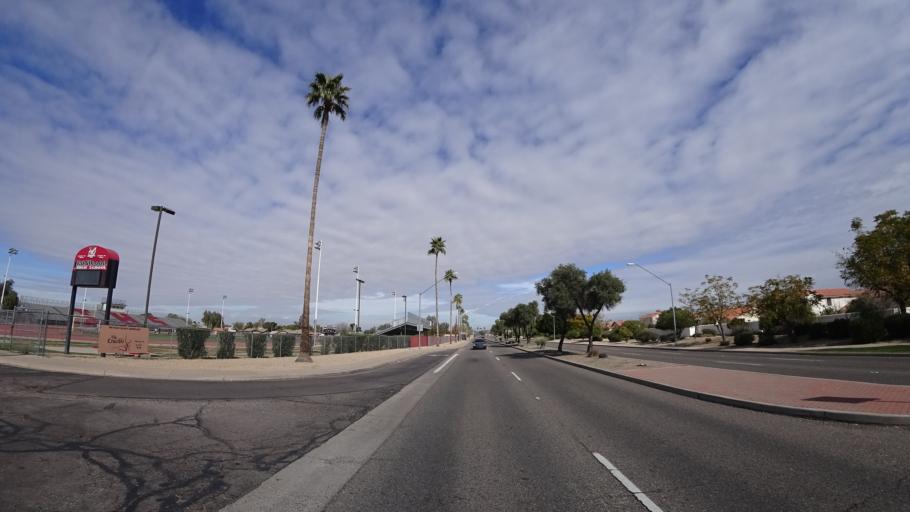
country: US
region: Arizona
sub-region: Maricopa County
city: Peoria
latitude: 33.6017
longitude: -112.1860
